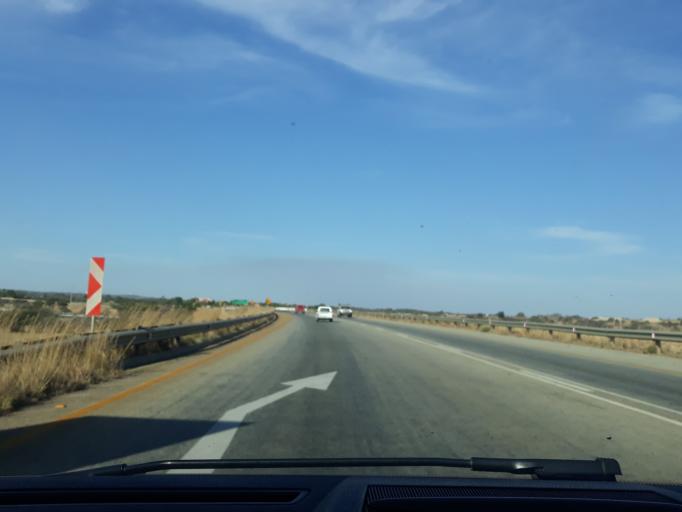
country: ZA
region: Limpopo
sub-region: Capricorn District Municipality
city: Polokwane
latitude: -23.9467
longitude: 29.4125
